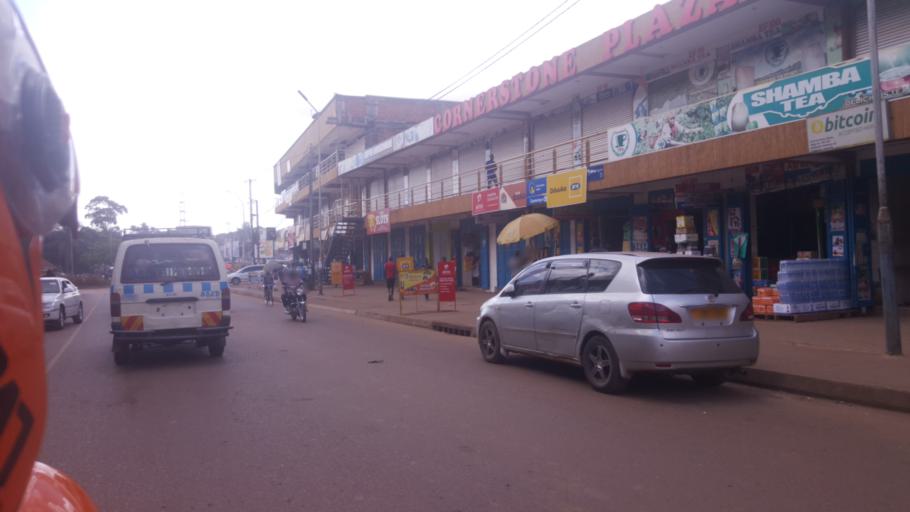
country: UG
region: Central Region
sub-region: Kampala District
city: Kampala
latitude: 0.3070
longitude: 32.5757
